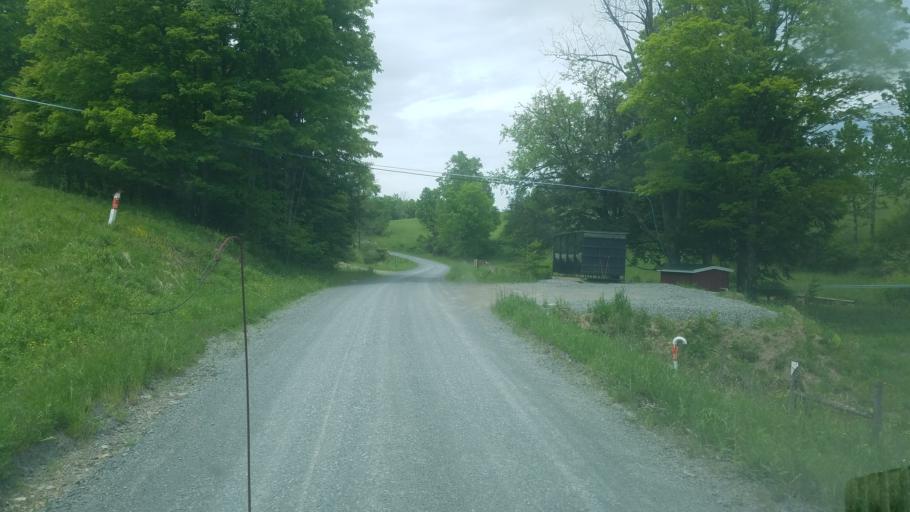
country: US
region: Pennsylvania
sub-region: Tioga County
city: Westfield
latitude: 41.8393
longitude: -77.6005
